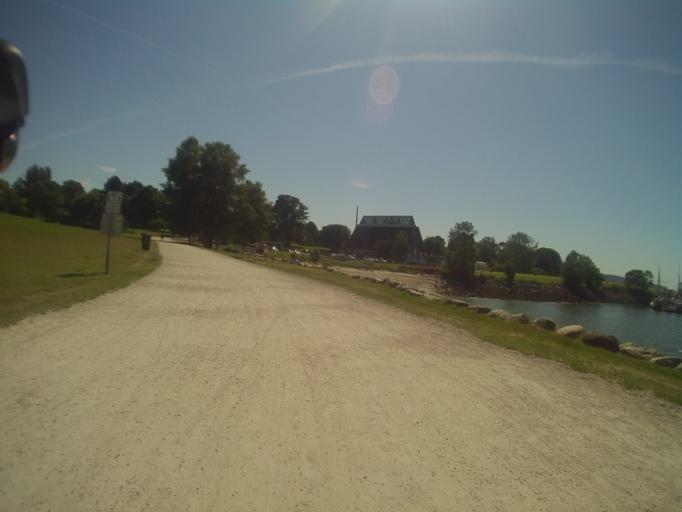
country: CA
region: British Columbia
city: West End
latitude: 49.2785
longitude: -123.1451
